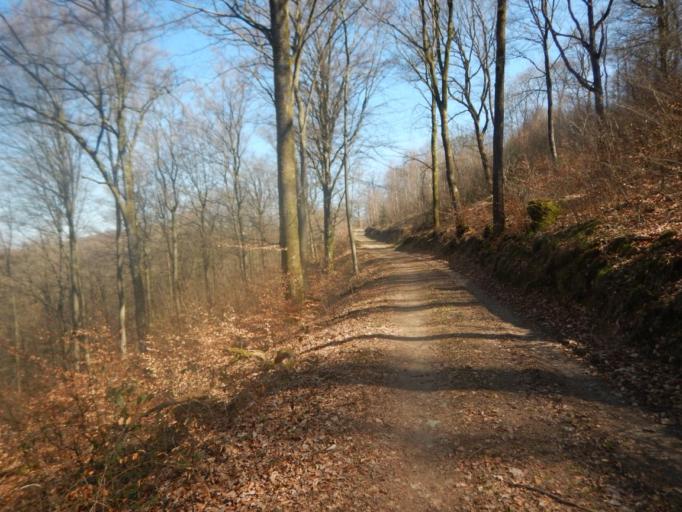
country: LU
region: Diekirch
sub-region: Canton de Wiltz
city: Wiltz
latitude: 49.9602
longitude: 5.9458
